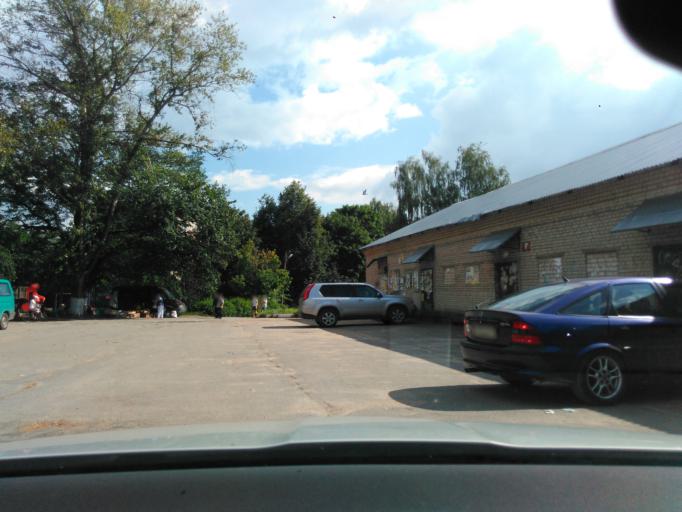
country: RU
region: Moskovskaya
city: Peshki
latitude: 56.1480
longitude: 37.0576
